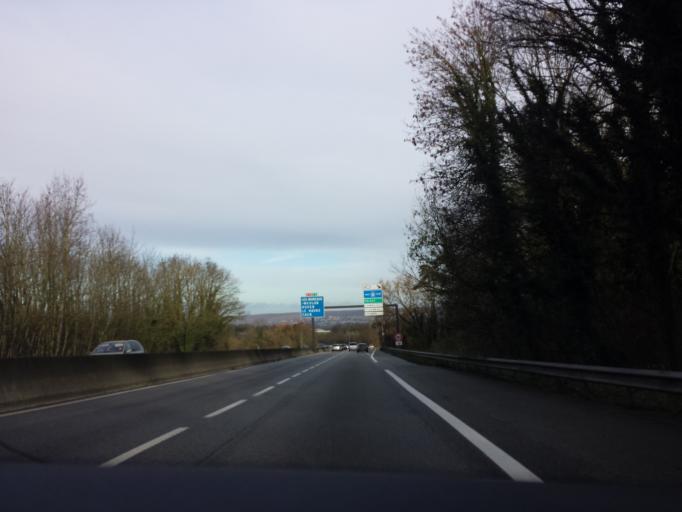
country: FR
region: Ile-de-France
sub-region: Departement des Yvelines
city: Orgeval
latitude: 48.9122
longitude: 2.0056
